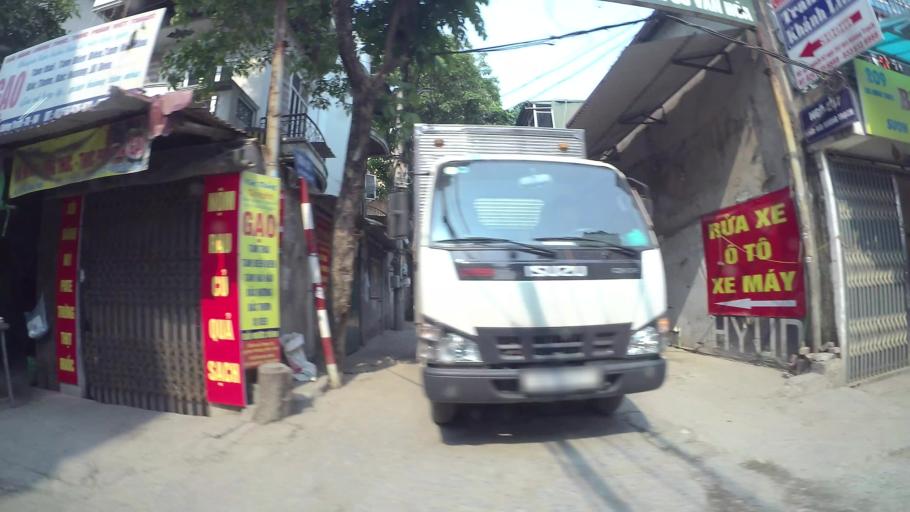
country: VN
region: Ha Noi
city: Thanh Xuan
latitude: 20.9872
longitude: 105.8186
